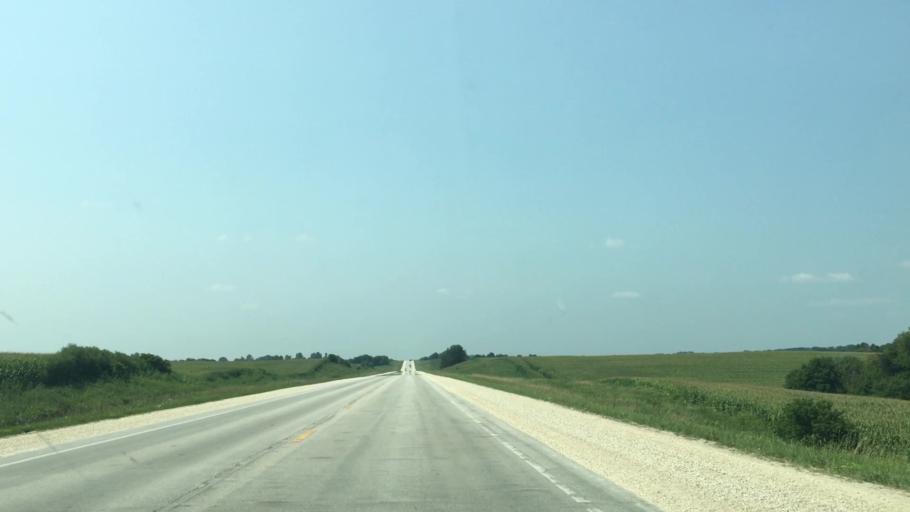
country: US
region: Iowa
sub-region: Winneshiek County
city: Decorah
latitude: 43.3711
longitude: -91.8101
